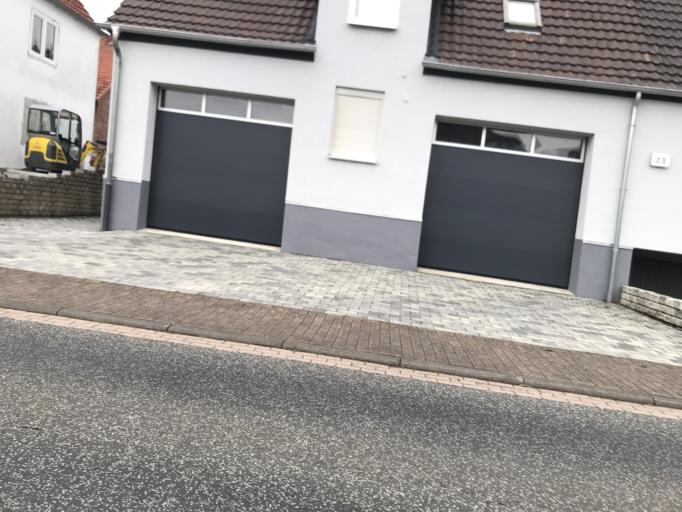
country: DE
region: Hesse
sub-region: Regierungsbezirk Kassel
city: Guxhagen
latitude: 51.2039
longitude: 9.4327
